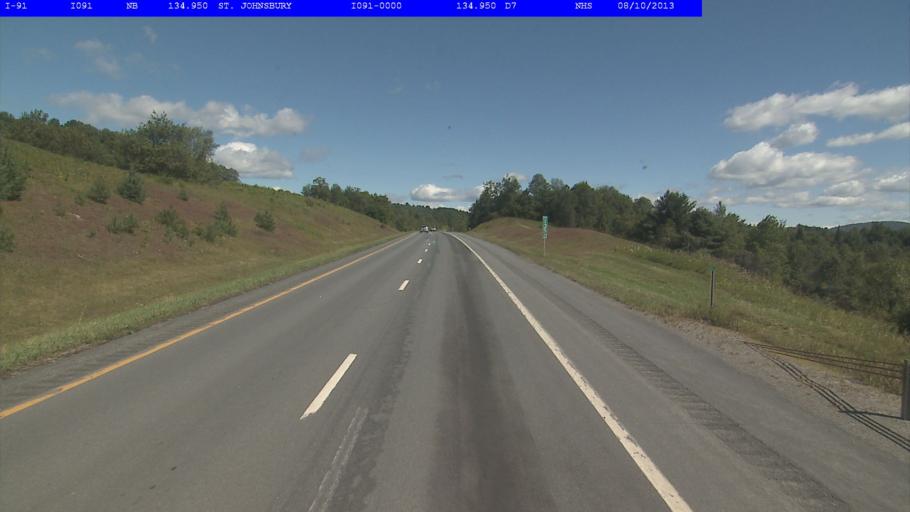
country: US
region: Vermont
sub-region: Caledonia County
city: Lyndon
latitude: 44.4879
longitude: -72.0212
